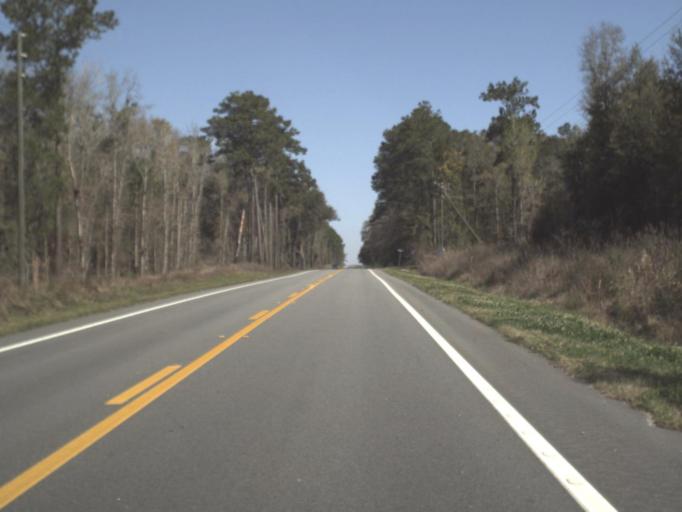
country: US
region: Florida
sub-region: Jefferson County
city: Monticello
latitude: 30.4291
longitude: -84.0197
